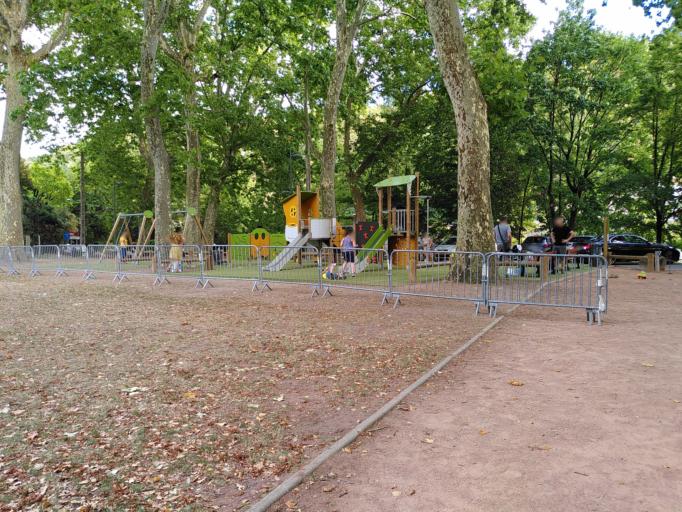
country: FR
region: Rhone-Alpes
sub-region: Departement du Rhone
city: Caluire-et-Cuire
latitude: 45.7961
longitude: 4.8325
